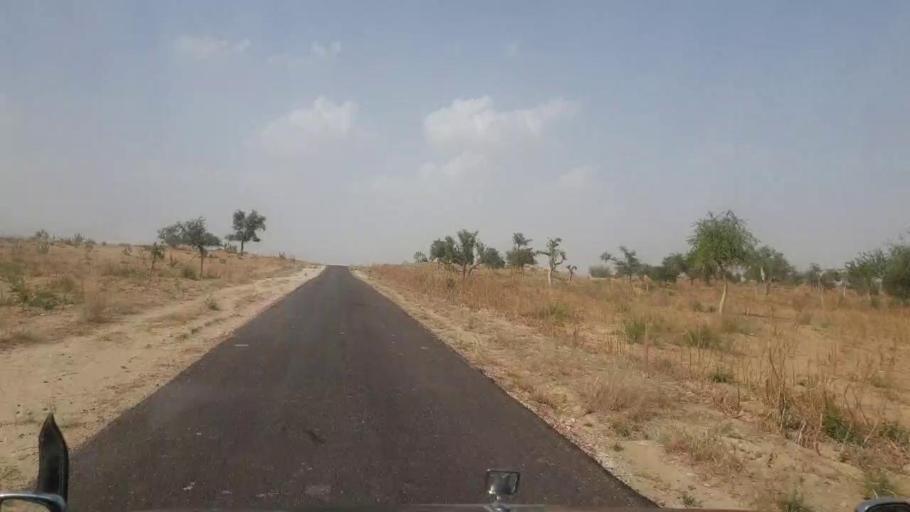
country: PK
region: Sindh
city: Islamkot
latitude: 25.1959
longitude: 70.2847
